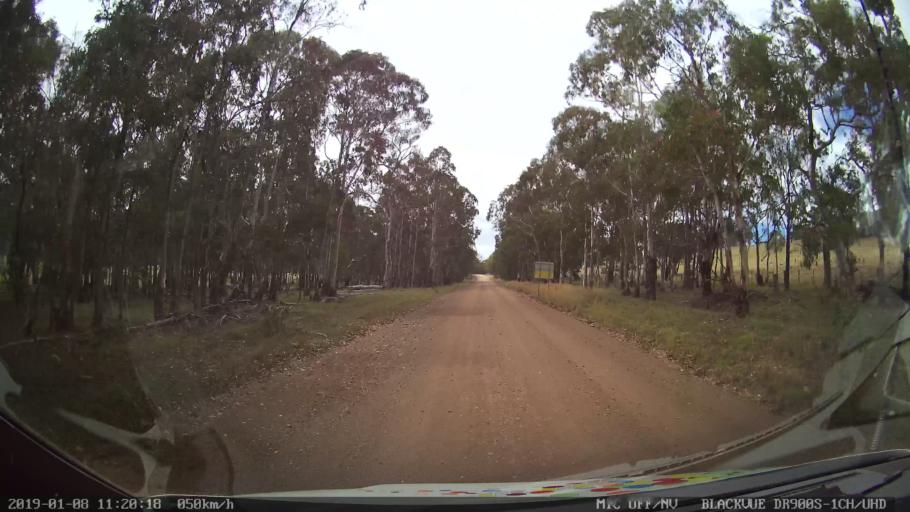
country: AU
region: New South Wales
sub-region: Guyra
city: Guyra
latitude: -30.2298
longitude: 151.5603
